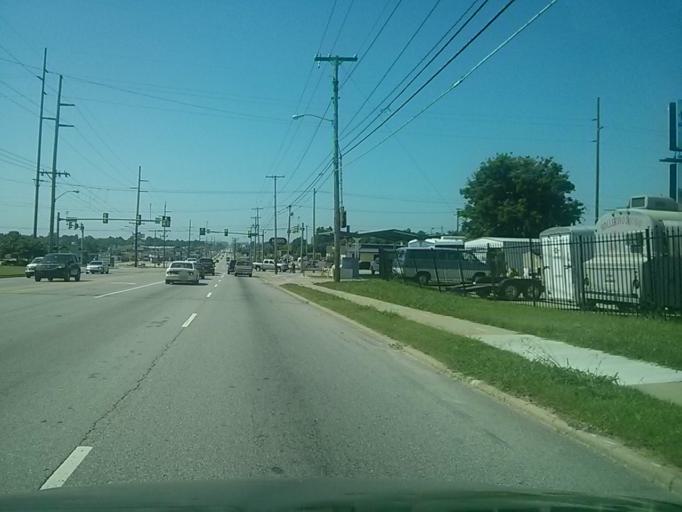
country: US
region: Oklahoma
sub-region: Tulsa County
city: Tulsa
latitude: 36.1416
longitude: -95.9047
